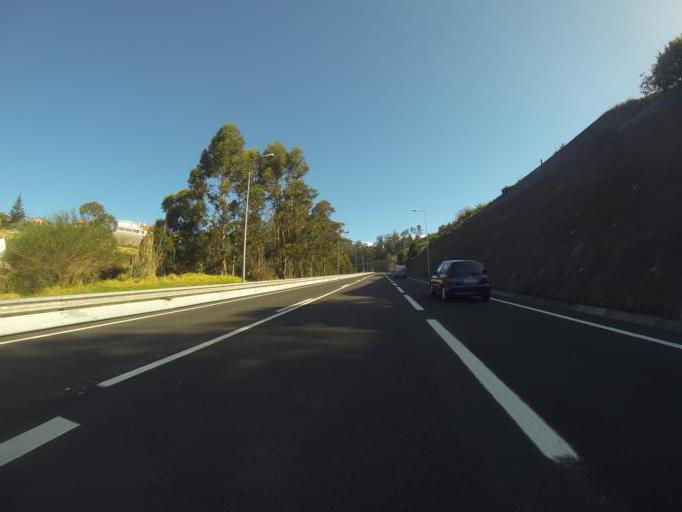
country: PT
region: Madeira
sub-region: Calheta
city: Estreito da Calheta
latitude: 32.7424
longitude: -17.1947
